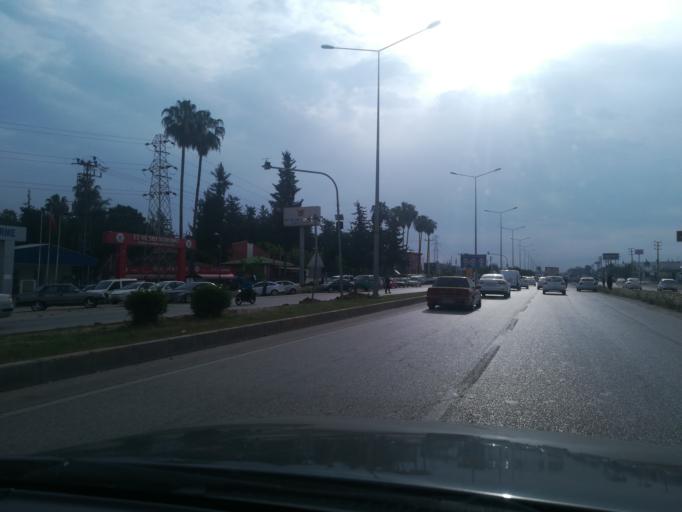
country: TR
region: Adana
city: Yuregir
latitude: 36.9836
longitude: 35.3791
